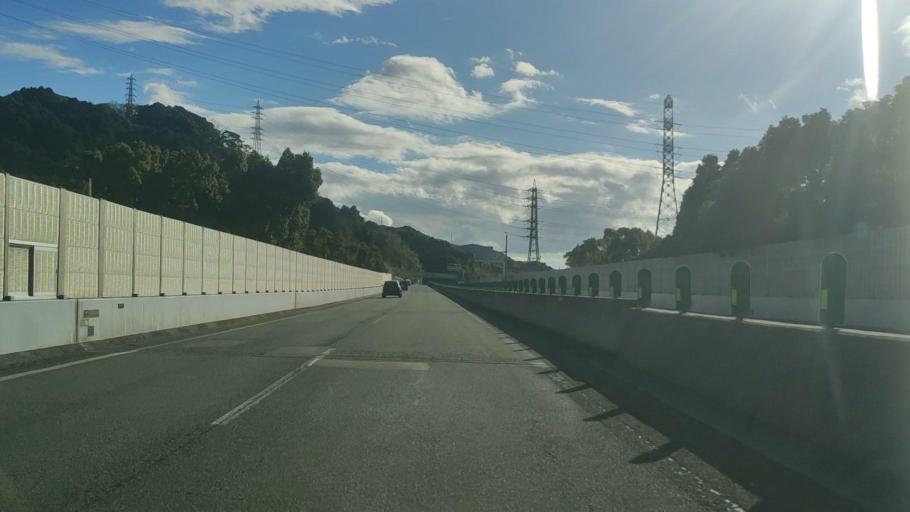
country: JP
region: Fukuoka
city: Kitakyushu
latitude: 33.8374
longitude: 130.7655
